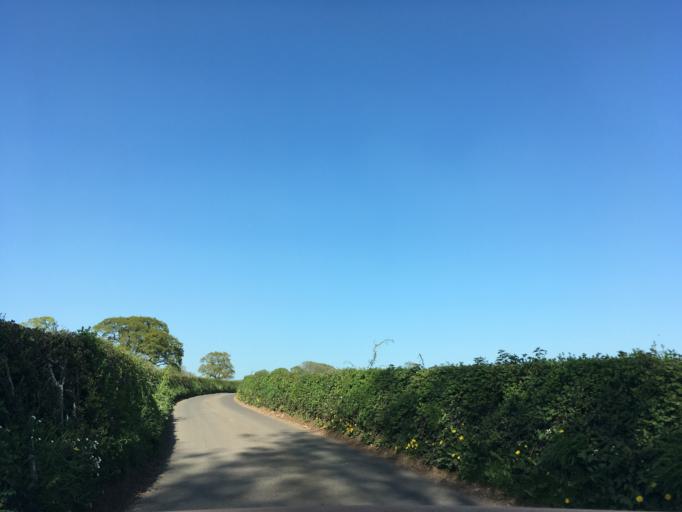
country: GB
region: Wales
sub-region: Monmouthshire
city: Rogiet
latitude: 51.6319
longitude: -2.7755
